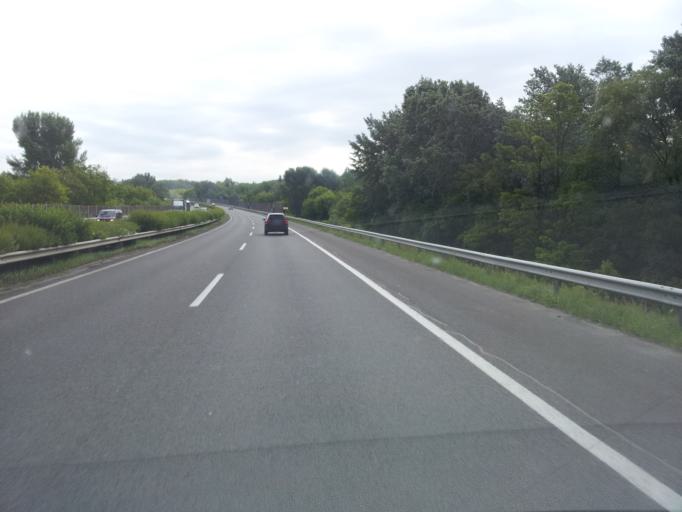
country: HU
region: Pest
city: Mogyorod
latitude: 47.5924
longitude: 19.2348
